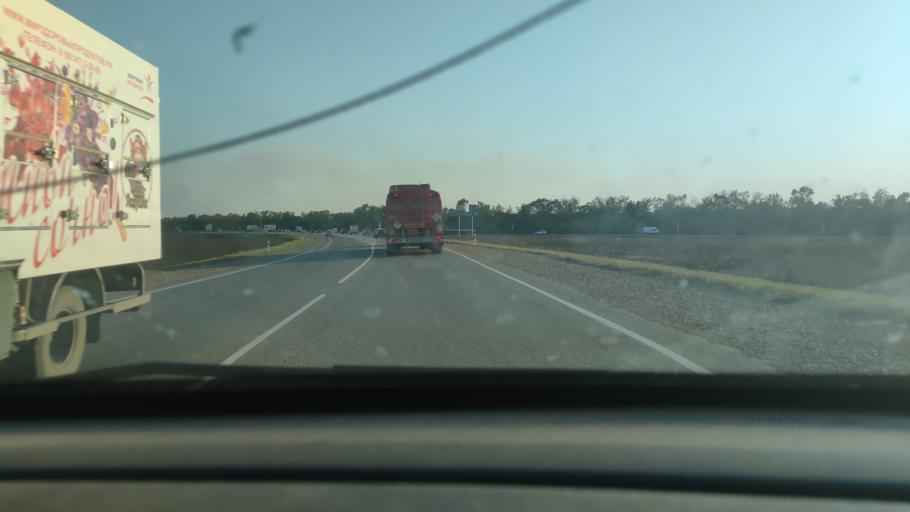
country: RU
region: Krasnodarskiy
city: Kanevskaya
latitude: 46.0285
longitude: 38.9745
